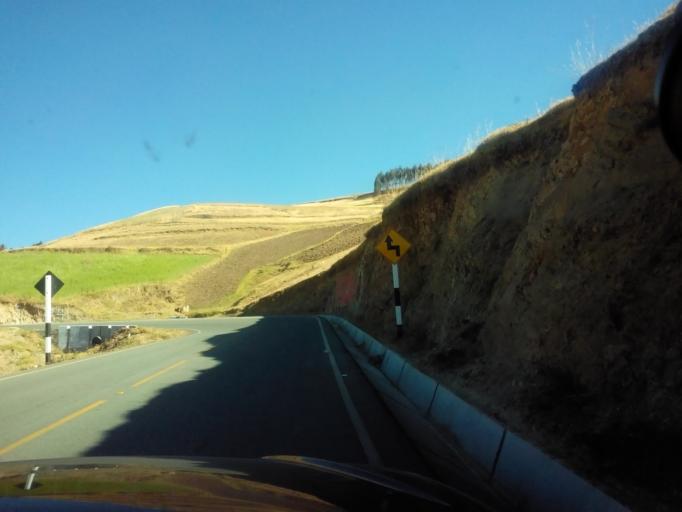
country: PE
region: Apurimac
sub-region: Provincia de Andahuaylas
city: Pacucha
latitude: -13.6570
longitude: -73.2897
